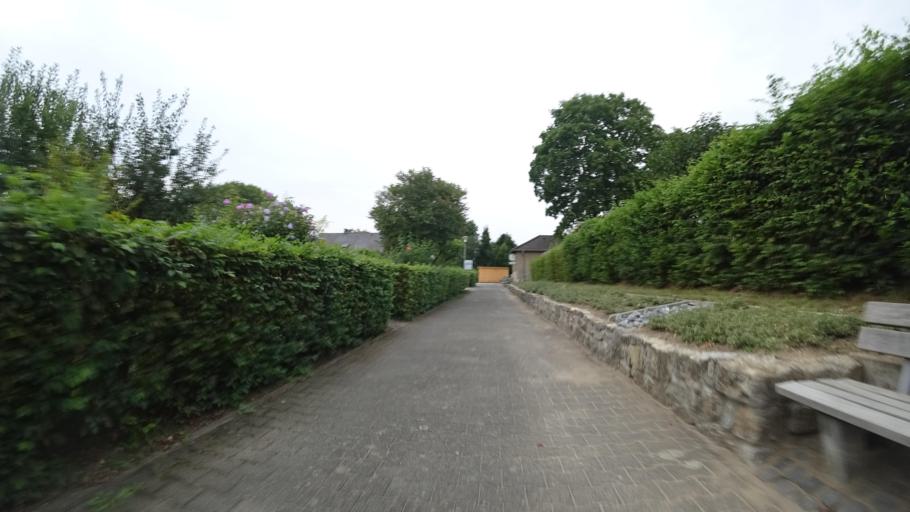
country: DE
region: North Rhine-Westphalia
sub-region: Regierungsbezirk Detmold
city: Guetersloh
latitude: 51.9175
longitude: 8.4152
